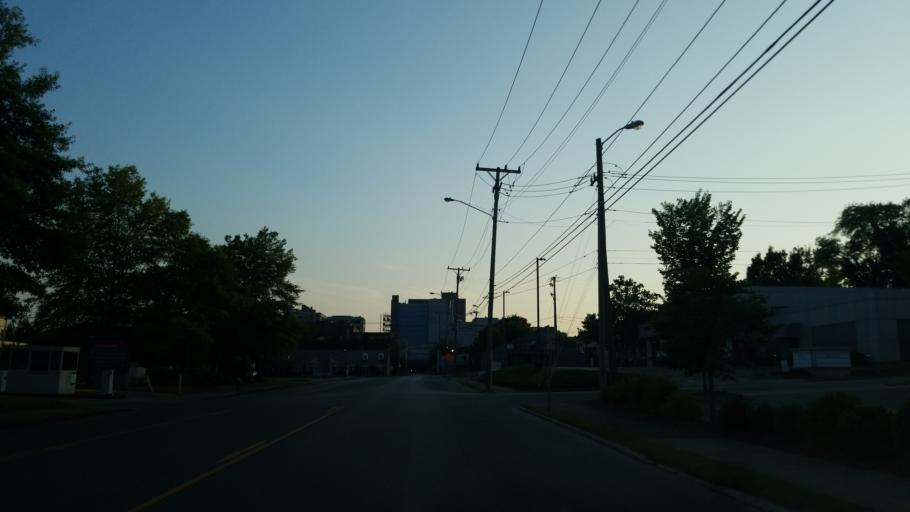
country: US
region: Tennessee
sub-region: Davidson County
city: Nashville
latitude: 36.1561
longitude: -86.8033
